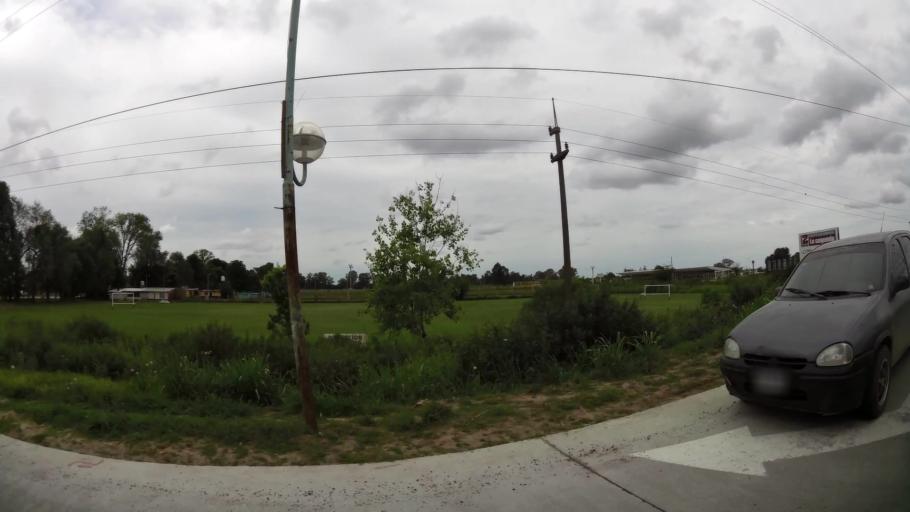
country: AR
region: Buenos Aires
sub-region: Partido de Zarate
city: Zarate
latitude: -34.1195
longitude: -59.0190
